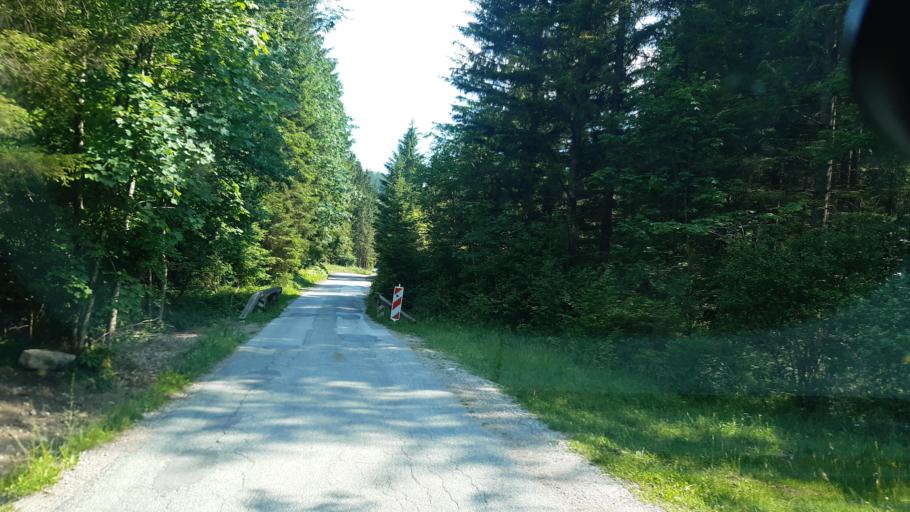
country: SI
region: Radovljica
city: Radovljica
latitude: 46.3877
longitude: 14.2175
